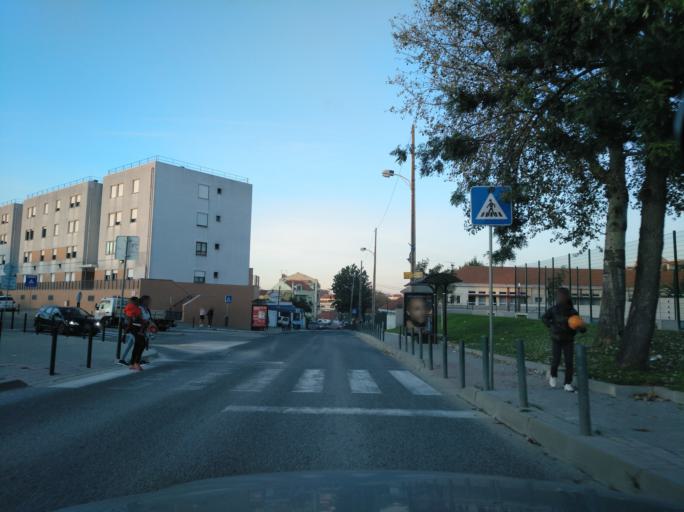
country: PT
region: Lisbon
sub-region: Odivelas
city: Olival do Basto
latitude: 38.7902
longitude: -9.1506
